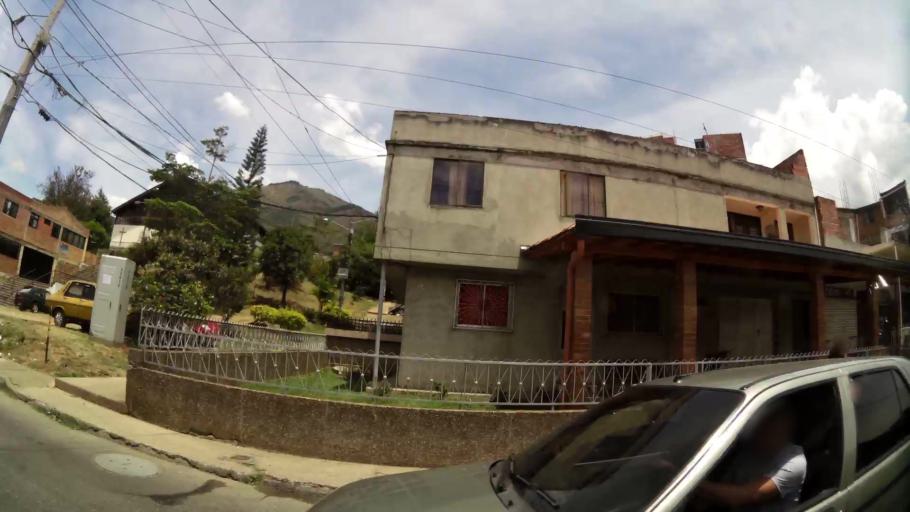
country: CO
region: Antioquia
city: Bello
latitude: 6.3450
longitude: -75.5567
